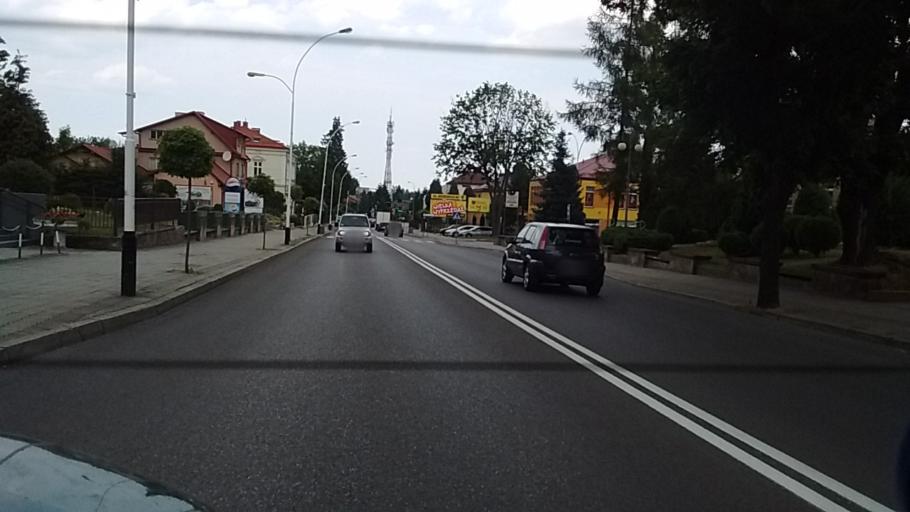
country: PL
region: Subcarpathian Voivodeship
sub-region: Powiat lezajski
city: Lezajsk
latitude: 50.2553
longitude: 22.4216
